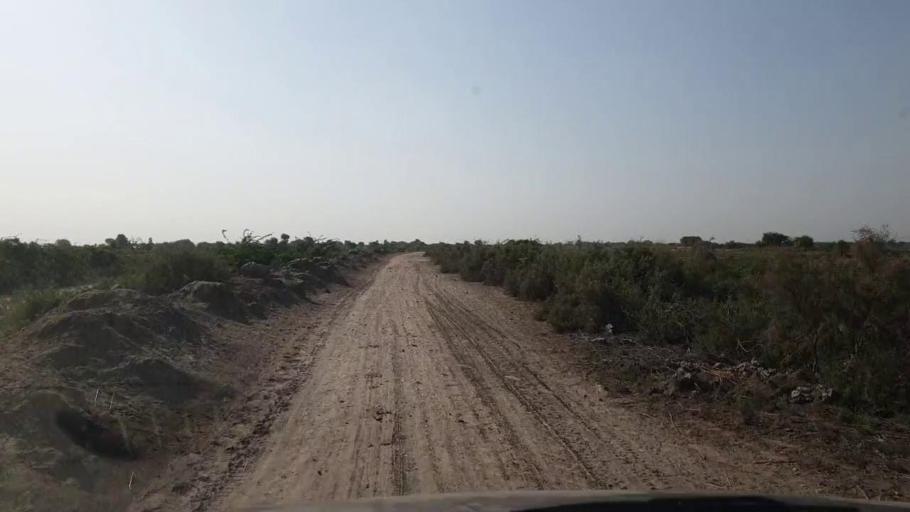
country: PK
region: Sindh
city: Kadhan
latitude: 24.6269
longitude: 69.0732
